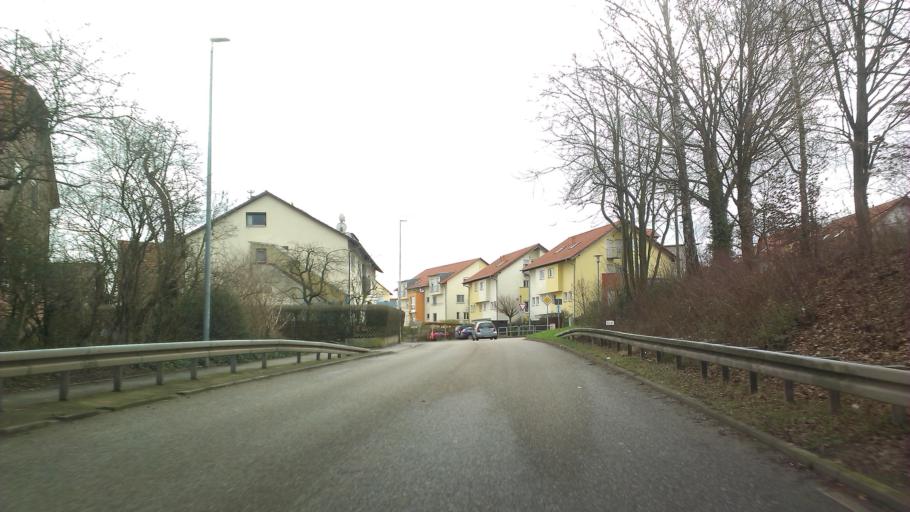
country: DE
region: Baden-Wuerttemberg
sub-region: Regierungsbezirk Stuttgart
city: Sersheim
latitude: 48.9620
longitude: 9.0097
